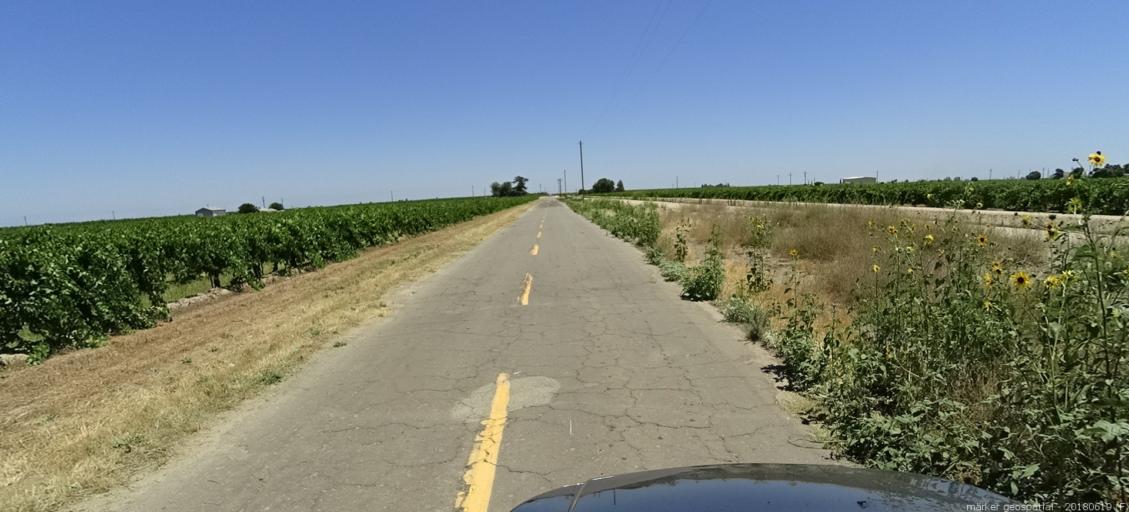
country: US
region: California
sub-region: Madera County
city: Parkwood
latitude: 36.8586
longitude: -120.0604
